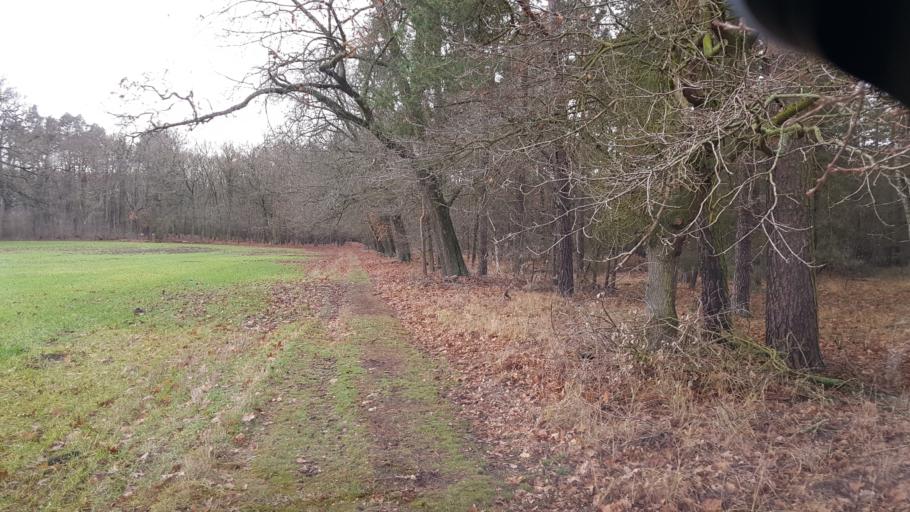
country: DE
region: Brandenburg
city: Altdobern
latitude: 51.6738
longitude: 14.0234
